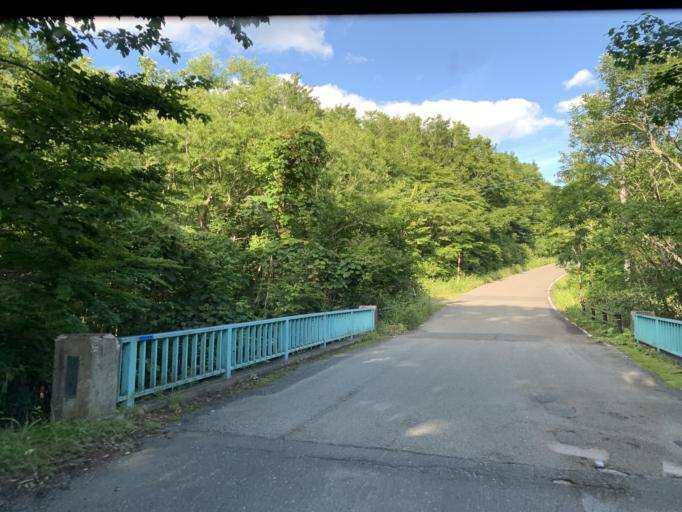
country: JP
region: Iwate
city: Ichinoseki
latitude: 38.9309
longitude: 140.8314
